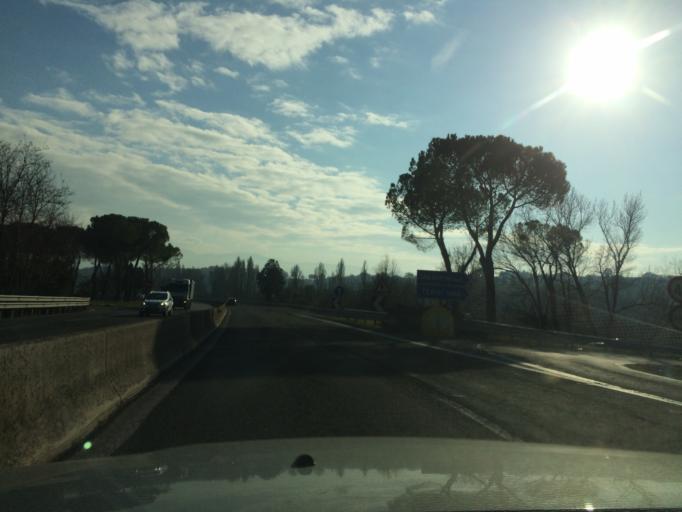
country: IT
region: Umbria
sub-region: Provincia di Terni
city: San Gemini
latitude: 42.5947
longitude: 12.5632
